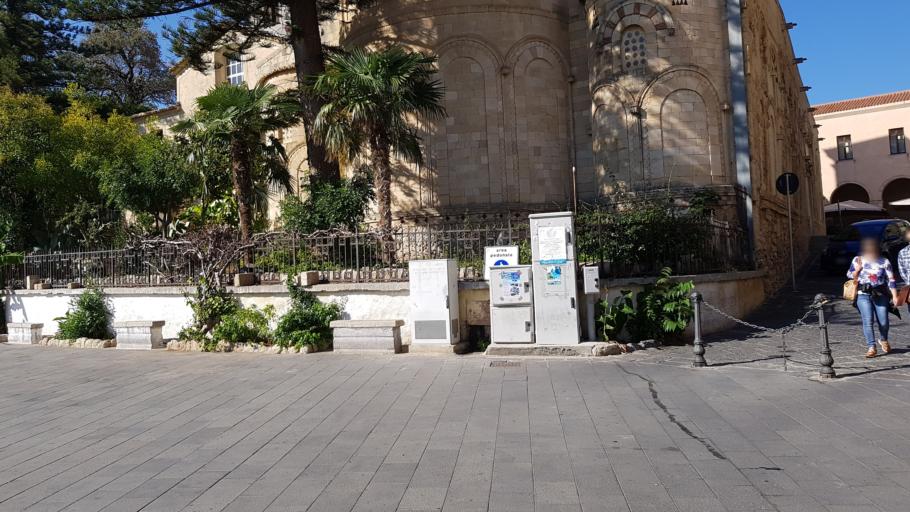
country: IT
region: Calabria
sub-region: Provincia di Vibo-Valentia
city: Tropea
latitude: 38.6780
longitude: 15.8992
